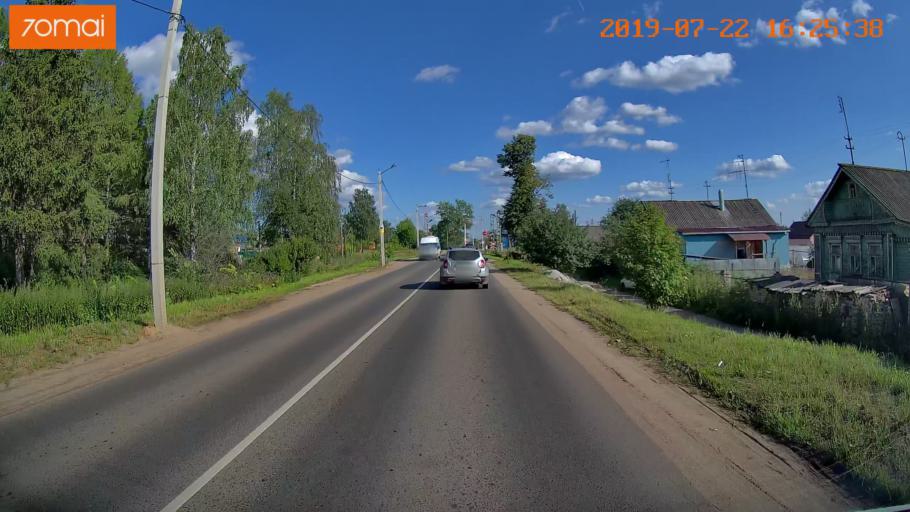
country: RU
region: Ivanovo
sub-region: Gorod Ivanovo
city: Ivanovo
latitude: 57.0523
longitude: 40.9269
